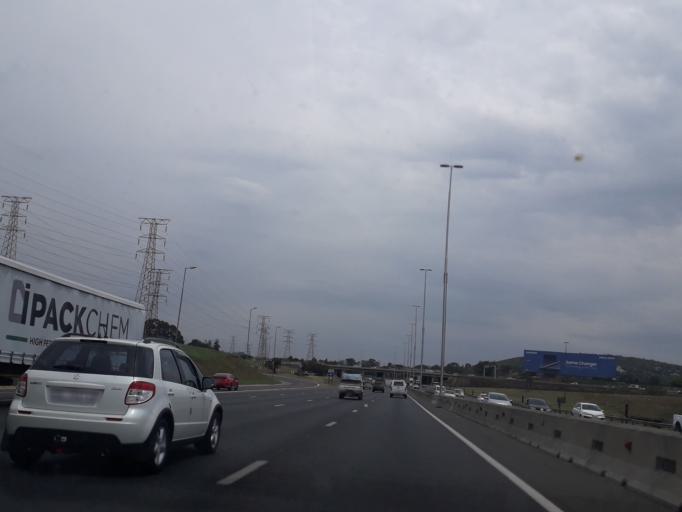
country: ZA
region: Gauteng
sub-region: City of Johannesburg Metropolitan Municipality
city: Modderfontein
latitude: -26.1449
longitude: 28.1316
